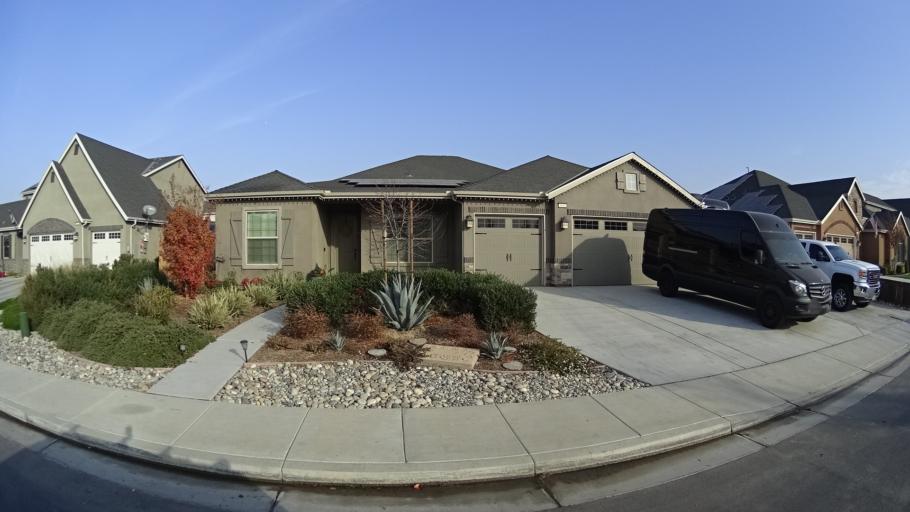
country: US
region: California
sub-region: Kern County
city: Greenacres
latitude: 35.4320
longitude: -119.1088
